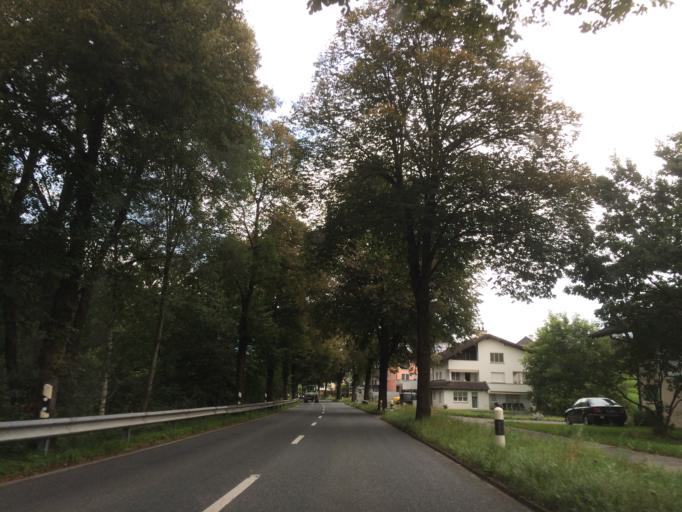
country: LI
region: Gamprin
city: Gamprin
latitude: 47.2139
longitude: 9.5028
